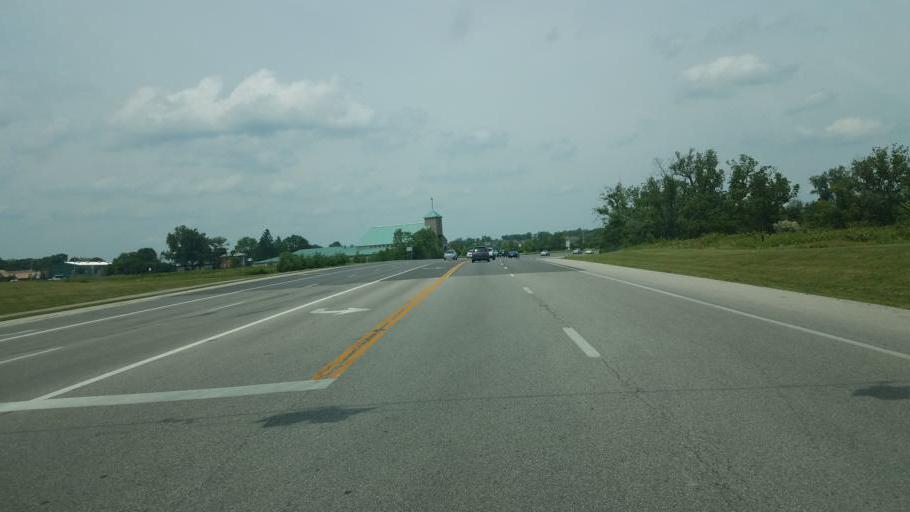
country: US
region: Ohio
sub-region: Delaware County
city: Powell
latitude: 40.1555
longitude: -83.1092
